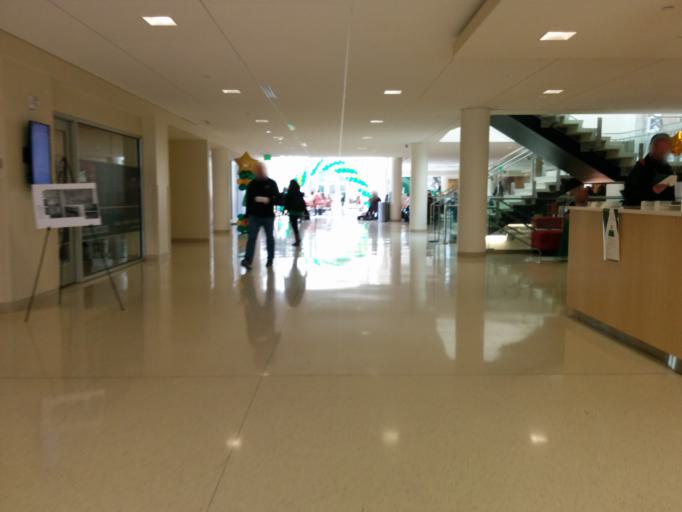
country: US
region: Colorado
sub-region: Larimer County
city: Fort Collins
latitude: 40.5745
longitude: -105.0841
